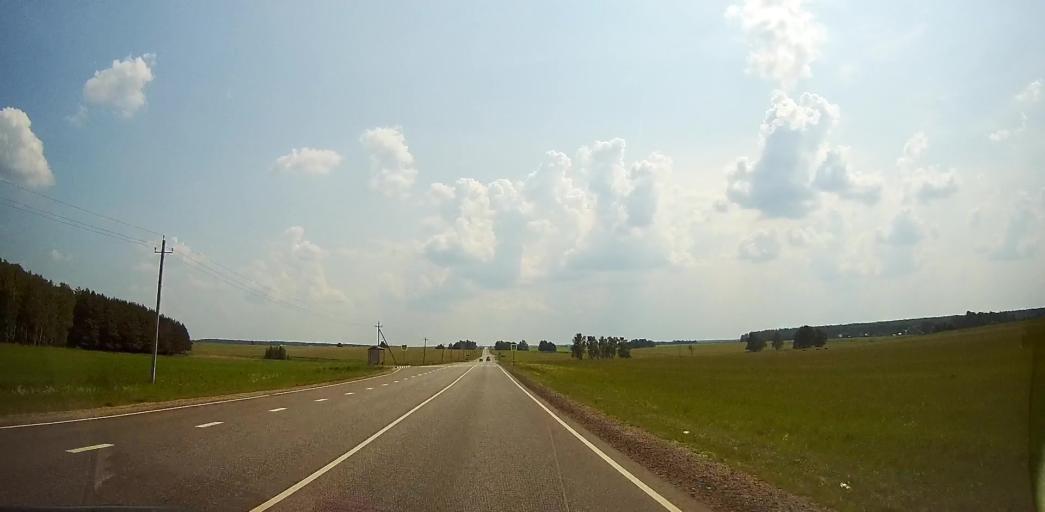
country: RU
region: Moskovskaya
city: Malino
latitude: 55.0501
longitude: 38.1462
